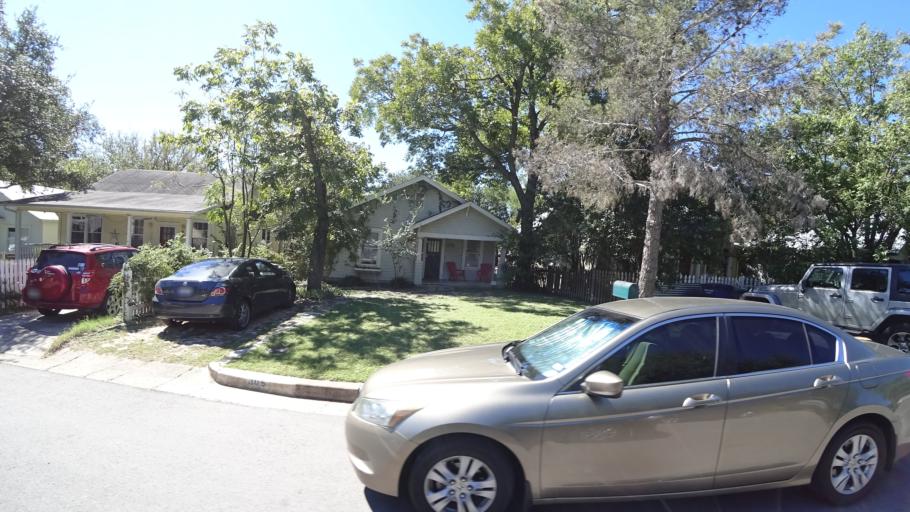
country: US
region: Texas
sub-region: Travis County
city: Austin
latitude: 30.2428
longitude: -97.7492
